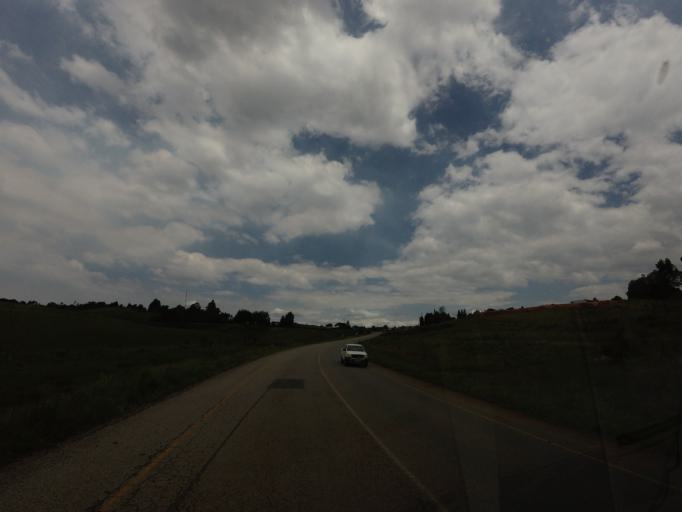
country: ZA
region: Mpumalanga
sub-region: Ehlanzeni District
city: Graksop
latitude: -24.9247
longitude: 30.8353
